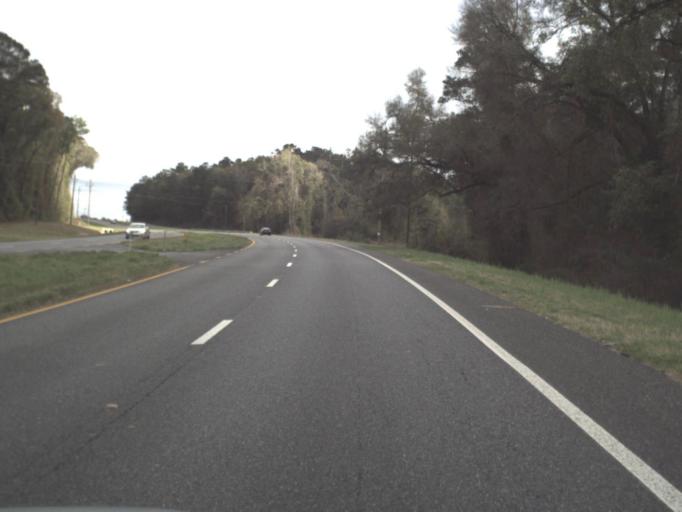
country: US
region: Florida
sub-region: Gadsden County
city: Havana
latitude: 30.5519
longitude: -84.3827
